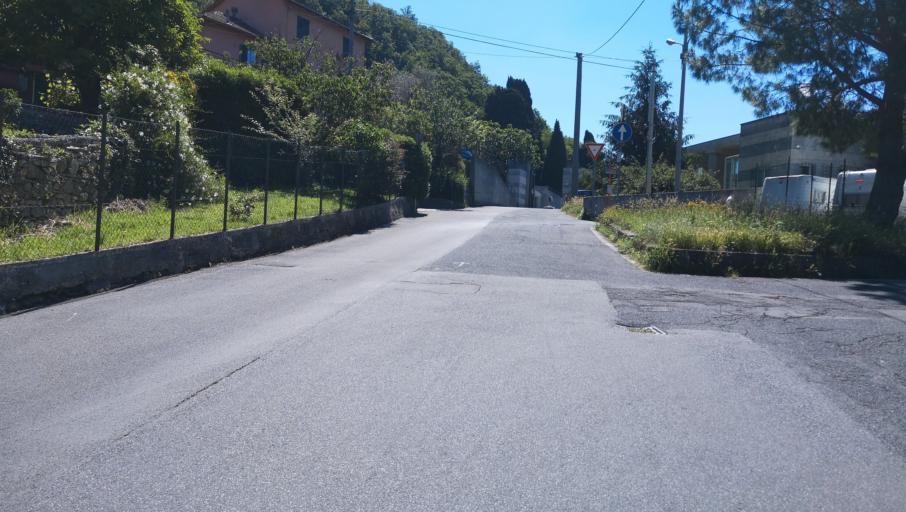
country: IT
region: Liguria
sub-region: Provincia di Genova
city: Piccarello
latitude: 44.4568
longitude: 8.9879
